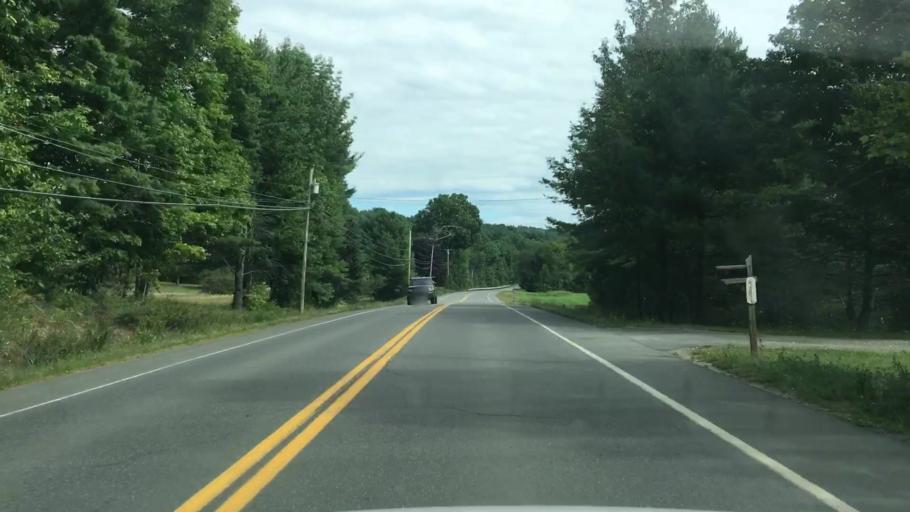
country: US
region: Maine
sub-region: Piscataquis County
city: Dover-Foxcroft
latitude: 45.2047
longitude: -69.1843
